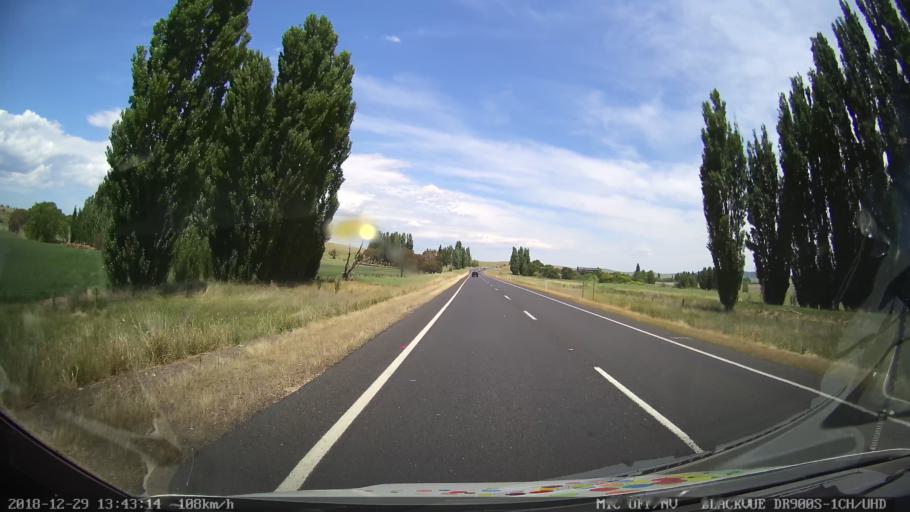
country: AU
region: New South Wales
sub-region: Cooma-Monaro
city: Cooma
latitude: -36.0692
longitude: 149.1588
